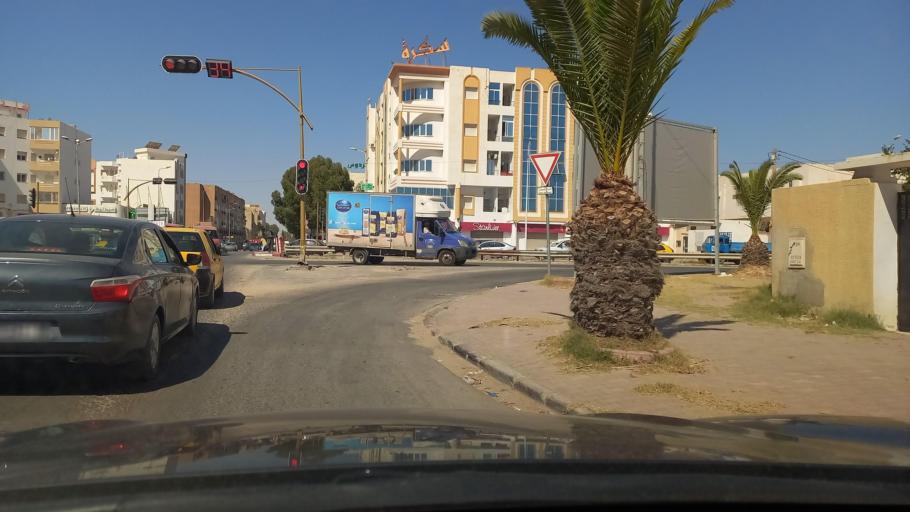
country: TN
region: Safaqis
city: Sfax
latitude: 34.7272
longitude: 10.7266
